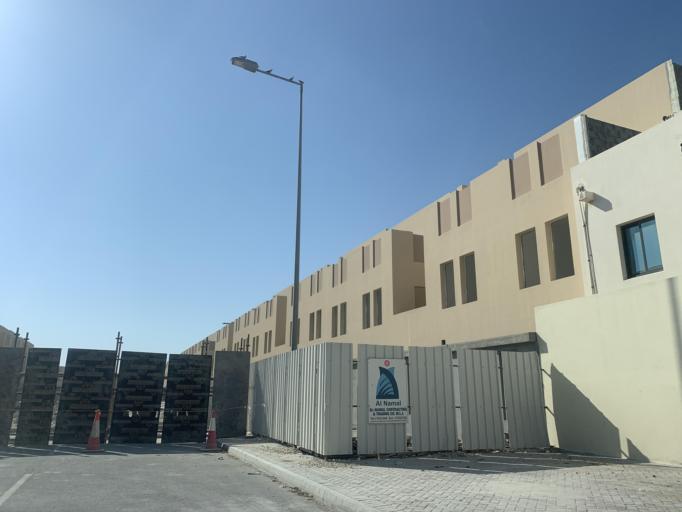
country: BH
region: Central Governorate
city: Madinat Hamad
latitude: 26.1225
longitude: 50.4831
